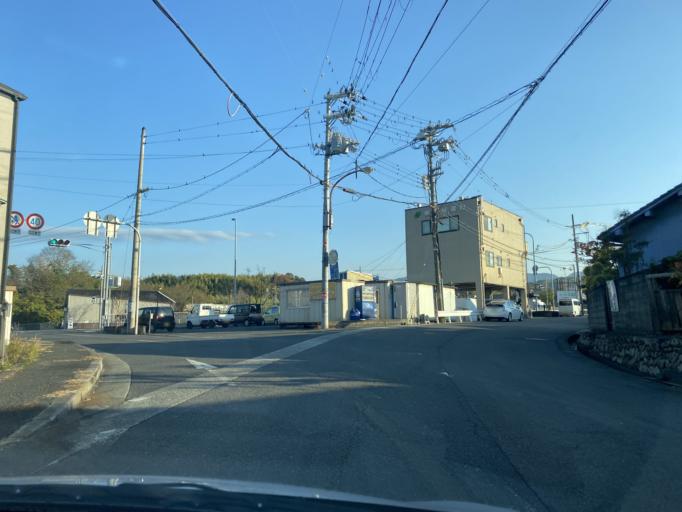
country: JP
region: Osaka
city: Izumi
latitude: 34.4242
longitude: 135.4392
